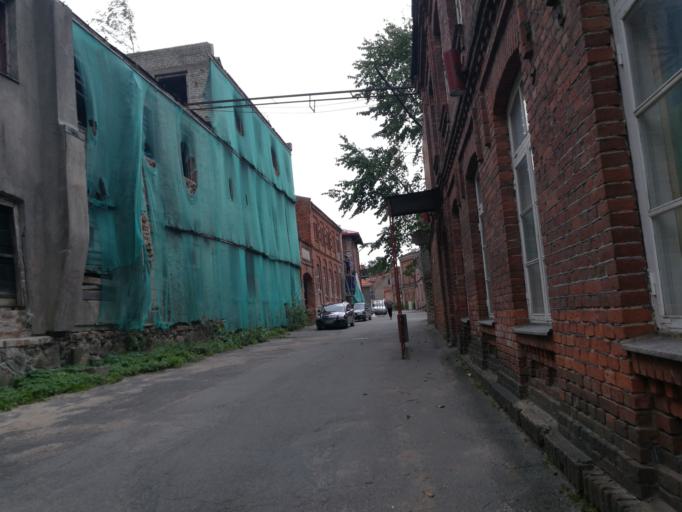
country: LV
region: Limbazu Rajons
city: Limbazi
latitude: 57.5148
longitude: 24.7107
